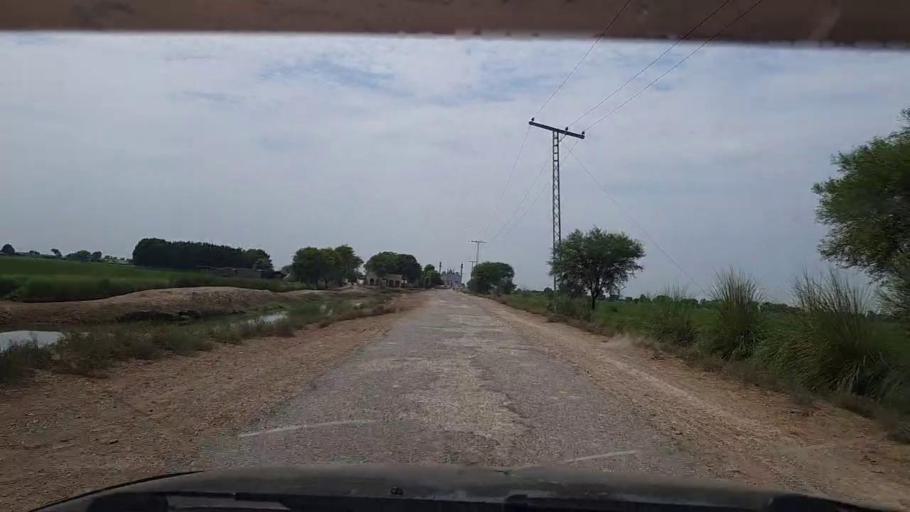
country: PK
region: Sindh
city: Thul
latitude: 28.2433
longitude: 68.7350
